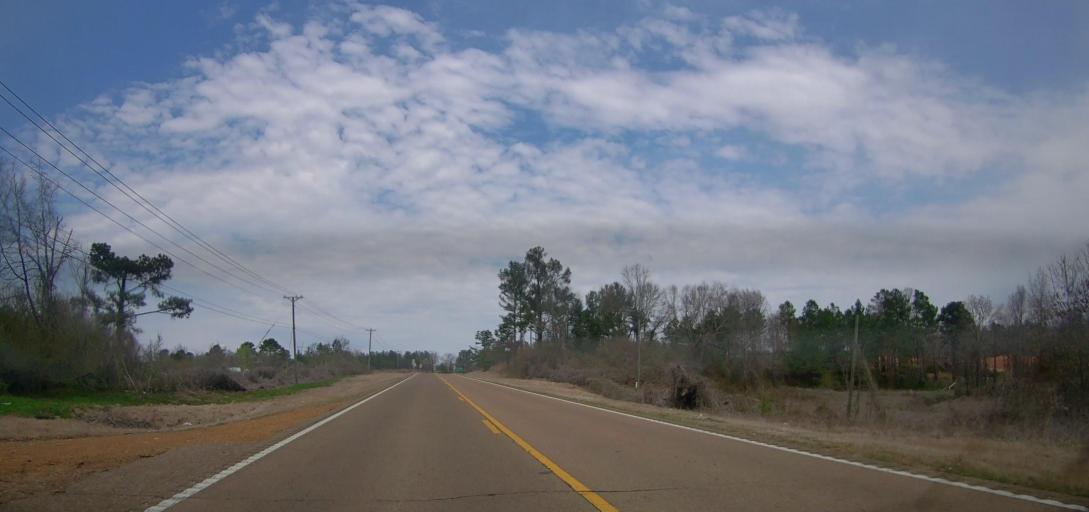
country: US
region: Mississippi
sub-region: Marshall County
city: Holly Springs
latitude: 34.7491
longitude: -89.4287
